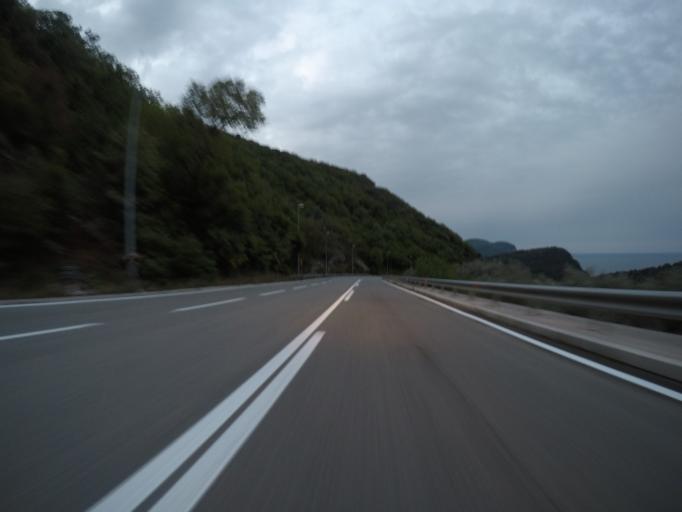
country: ME
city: Petrovac na Moru
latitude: 42.2084
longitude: 18.9481
